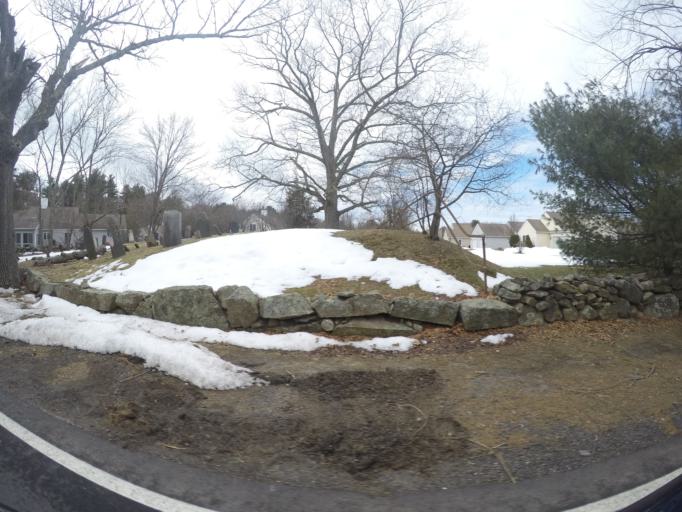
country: US
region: Massachusetts
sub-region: Bristol County
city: Easton
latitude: 42.0380
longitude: -71.1229
